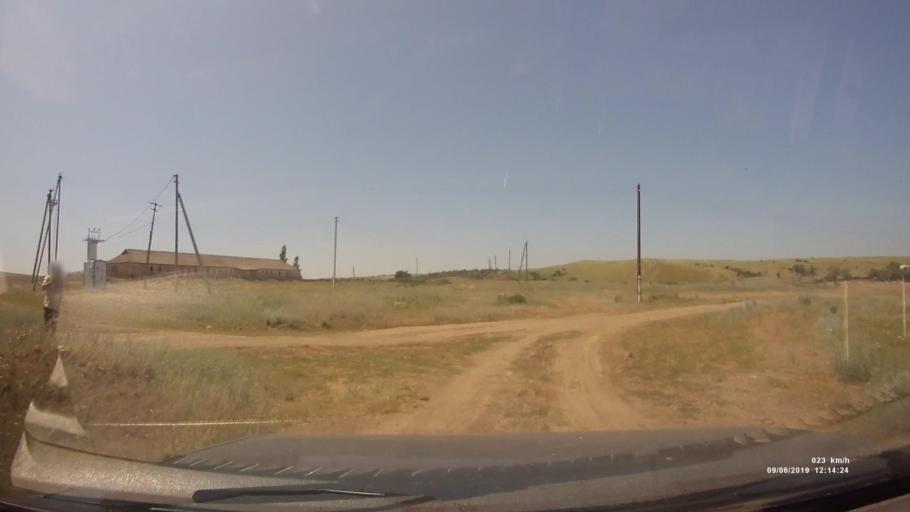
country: RU
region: Rostov
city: Staraya Stanitsa
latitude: 48.2518
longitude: 40.3215
